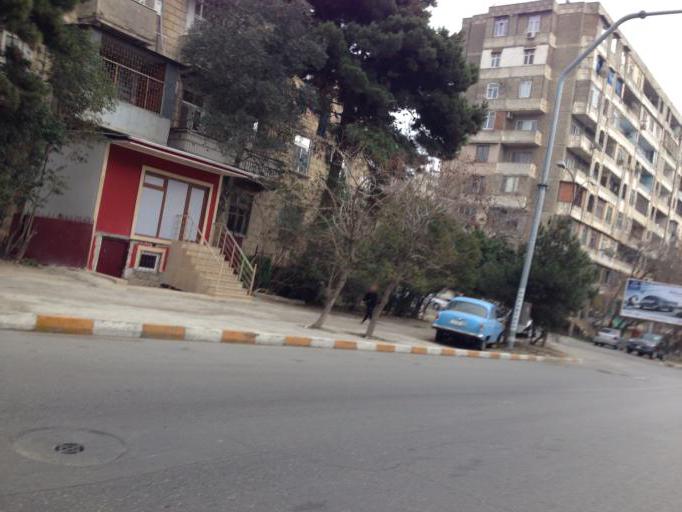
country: AZ
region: Baki
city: Baku
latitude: 40.3928
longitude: 49.8609
